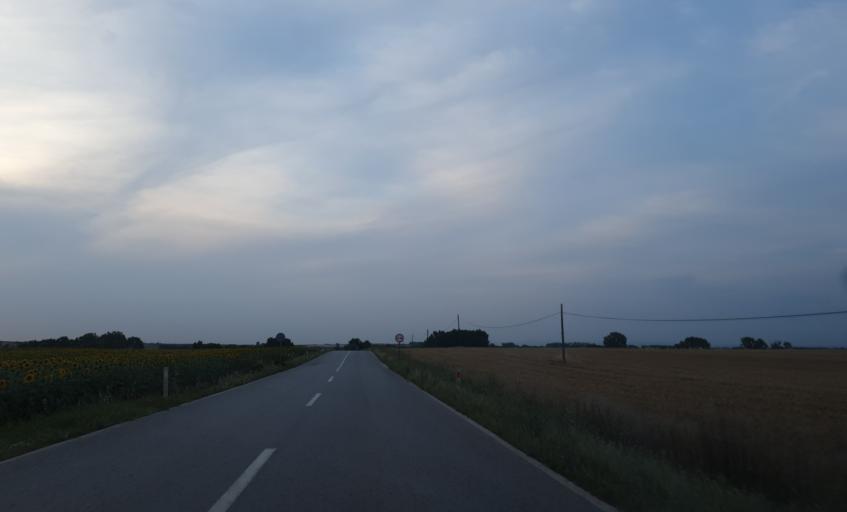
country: TR
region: Kirklareli
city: Buyukkaristiran
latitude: 41.3561
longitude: 27.6068
